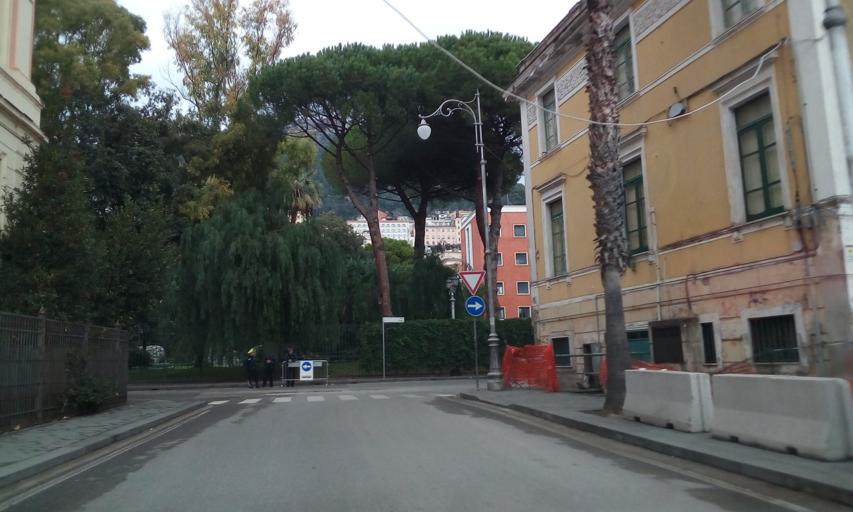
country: IT
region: Campania
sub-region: Provincia di Salerno
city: Vietri sul Mare
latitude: 40.6777
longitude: 14.7538
